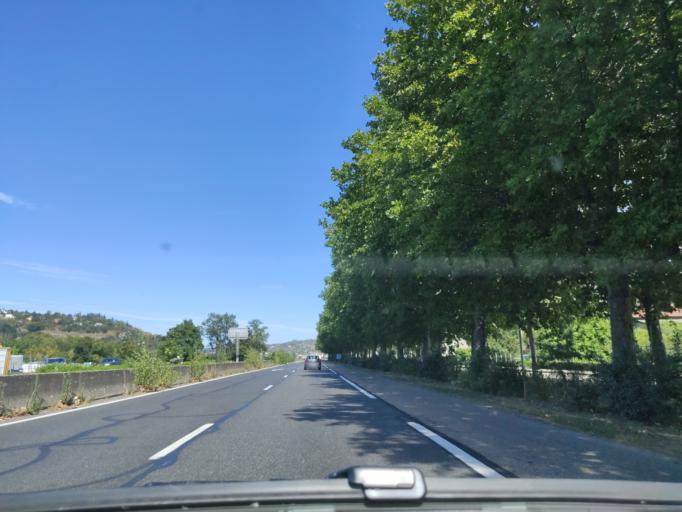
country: FR
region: Rhone-Alpes
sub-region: Departement du Rhone
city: Saint-Cyr-sur-le-Rhone
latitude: 45.5071
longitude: 4.8526
